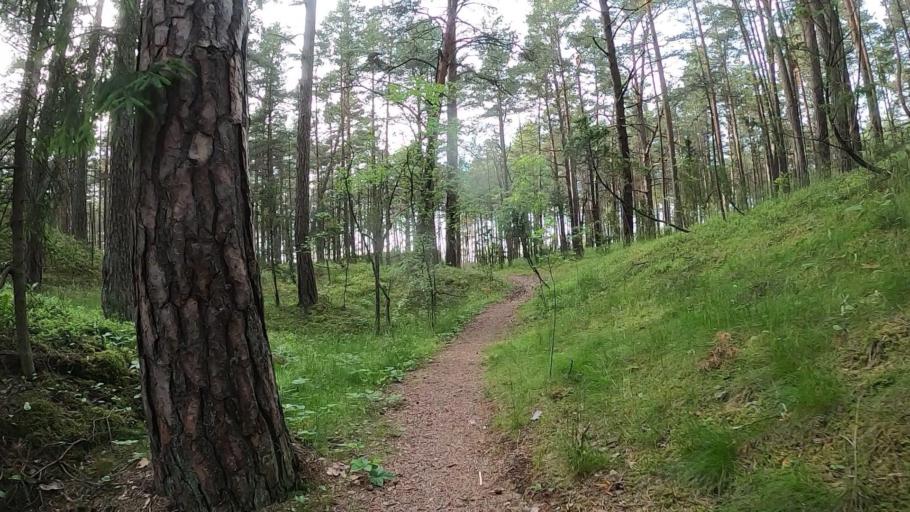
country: LV
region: Riga
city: Jaunciems
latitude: 57.0907
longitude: 24.1385
